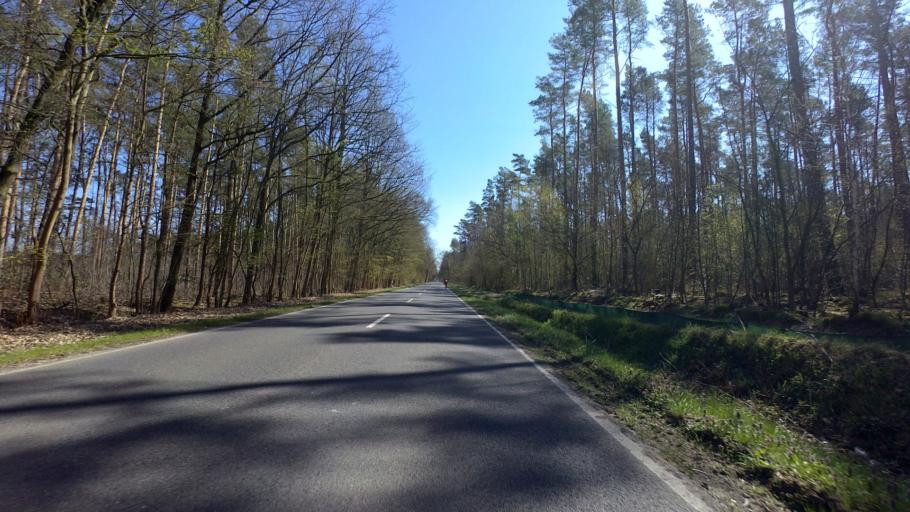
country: DE
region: Brandenburg
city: Schulzendorf
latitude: 52.3400
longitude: 13.5771
